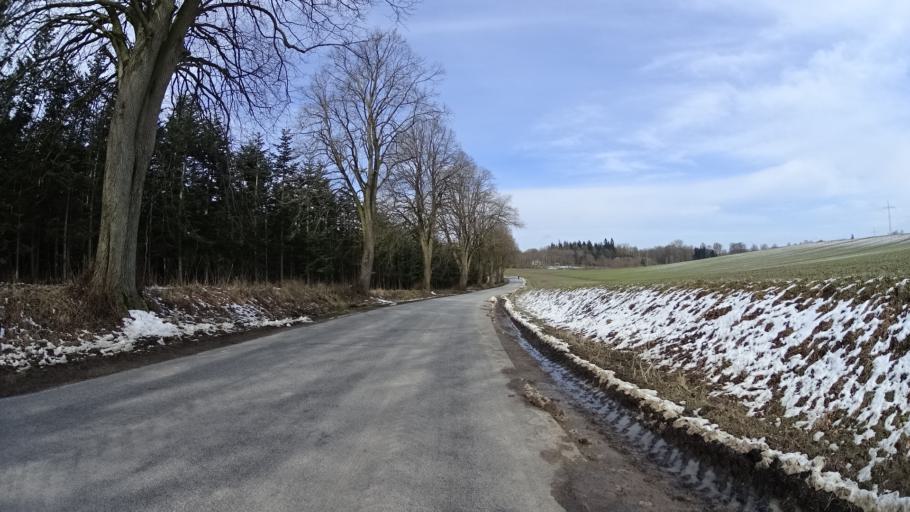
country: DE
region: Schleswig-Holstein
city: Stolpe
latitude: 54.1513
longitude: 10.2337
